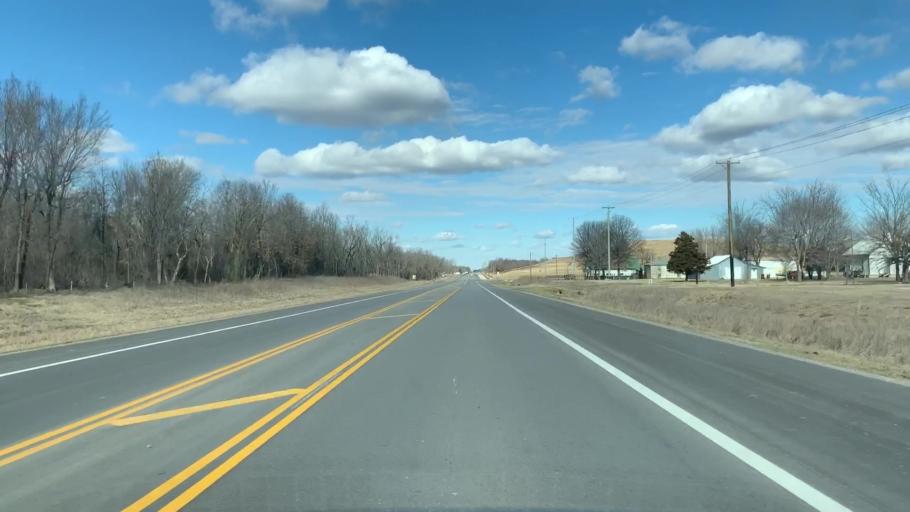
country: US
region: Kansas
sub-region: Cherokee County
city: Columbus
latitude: 37.2336
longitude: -94.8319
